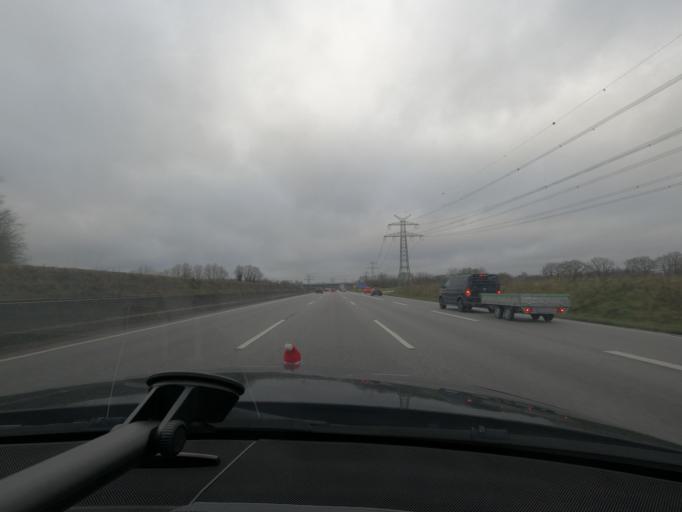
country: DE
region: Schleswig-Holstein
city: Alveslohe
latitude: 53.8011
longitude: 9.9304
